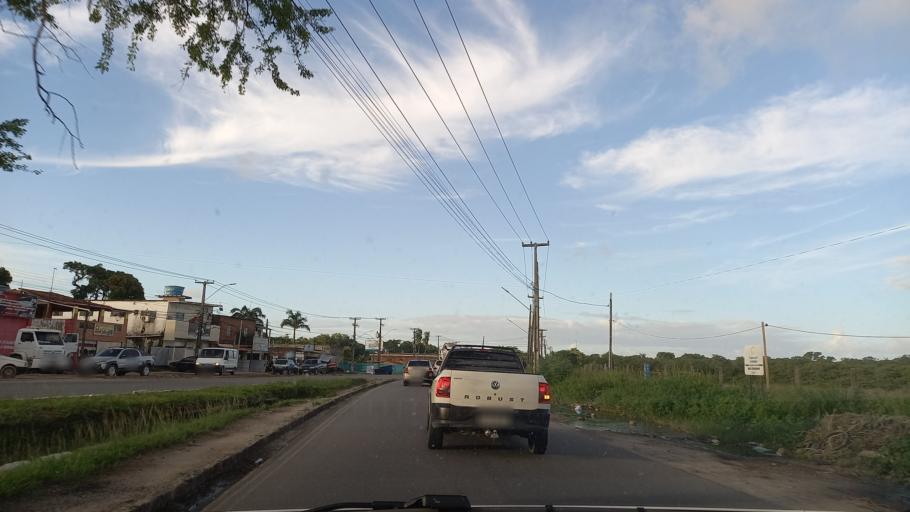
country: BR
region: Pernambuco
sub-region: Jaboatao Dos Guararapes
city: Jaboatao
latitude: -8.2333
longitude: -34.9776
